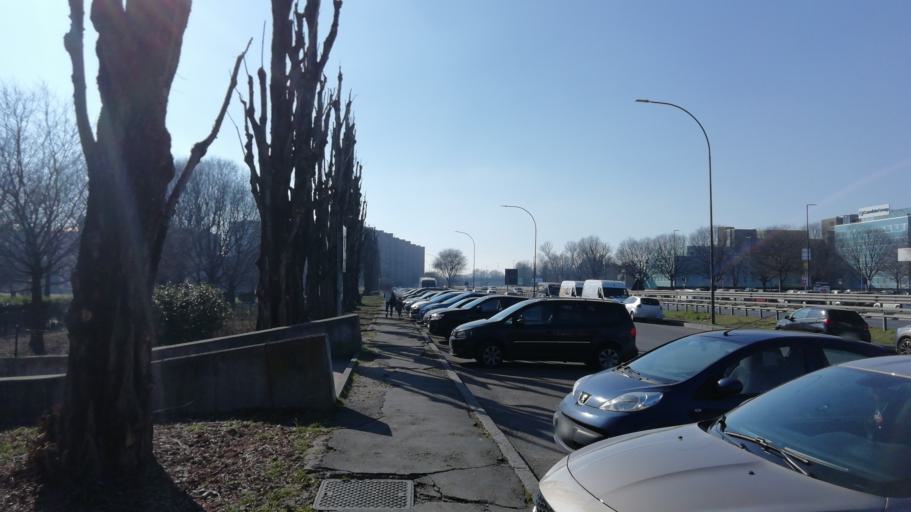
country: IT
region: Lombardy
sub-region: Citta metropolitana di Milano
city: Romano Banco
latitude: 45.4408
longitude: 9.1115
